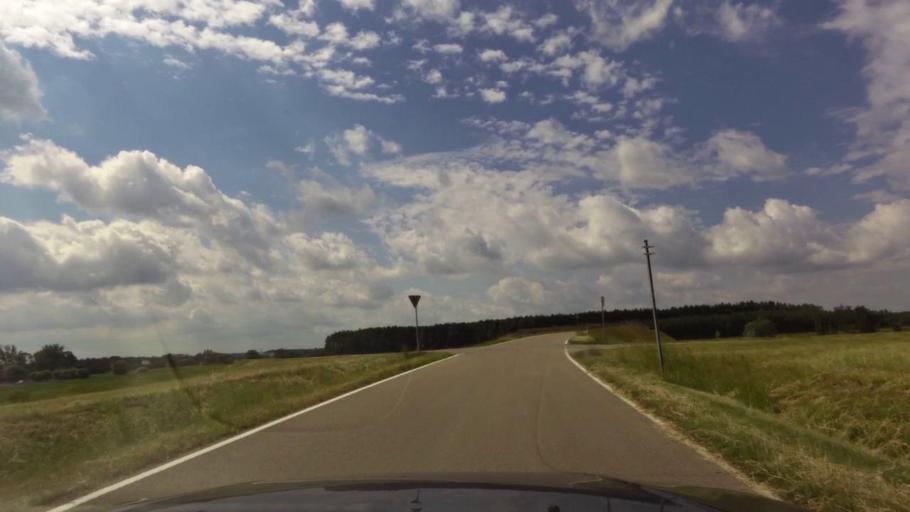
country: PL
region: West Pomeranian Voivodeship
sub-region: Powiat pyrzycki
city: Lipiany
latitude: 52.9597
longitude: 14.9314
